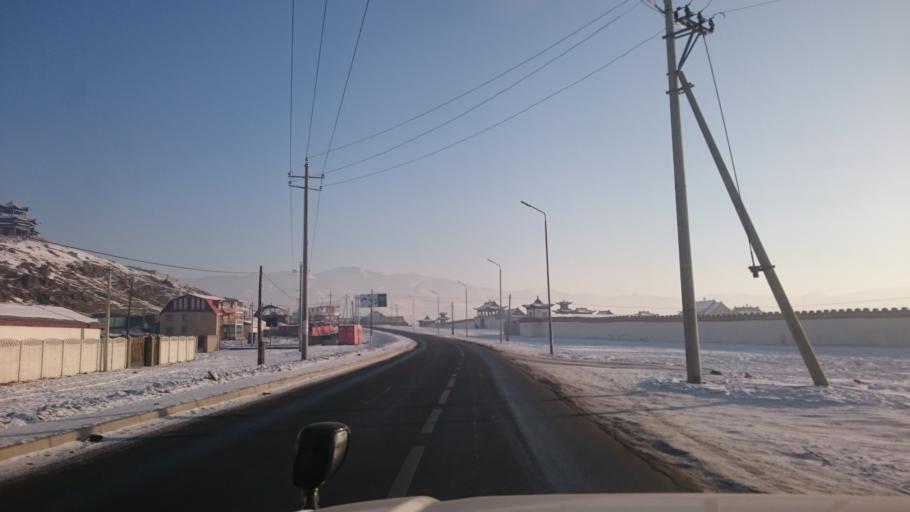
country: MN
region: Ulaanbaatar
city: Ulaanbaatar
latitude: 47.9244
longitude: 107.1376
